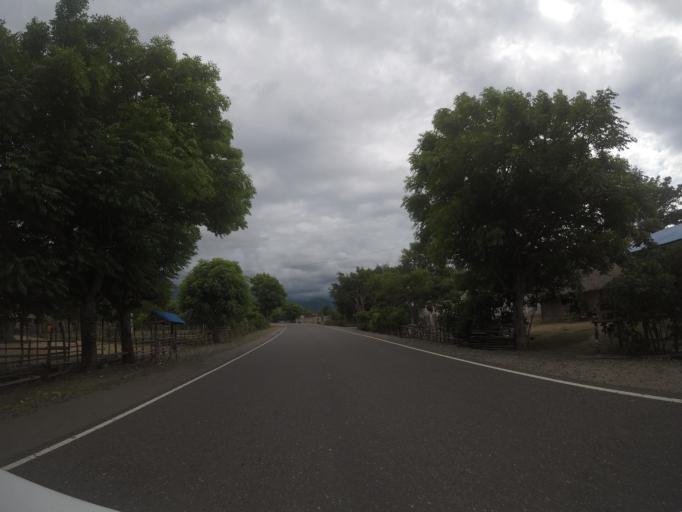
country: TL
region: Liquica
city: Maubara
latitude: -8.7687
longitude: 125.0994
